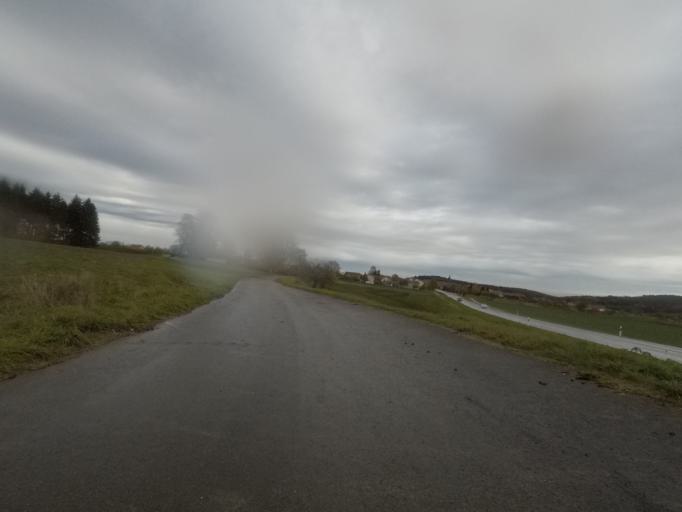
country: DE
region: Baden-Wuerttemberg
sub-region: Tuebingen Region
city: Sankt Johann
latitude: 48.4391
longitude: 9.3147
